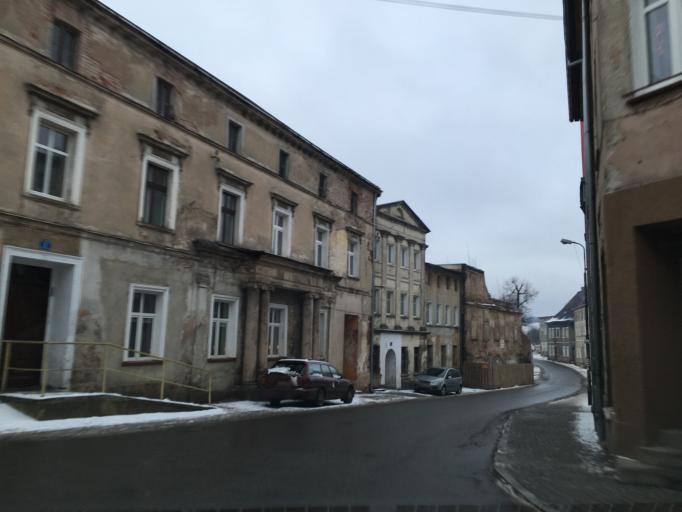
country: PL
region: Lower Silesian Voivodeship
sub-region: Powiat kamiennogorski
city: Krzeszow
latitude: 50.6667
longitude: 16.0687
